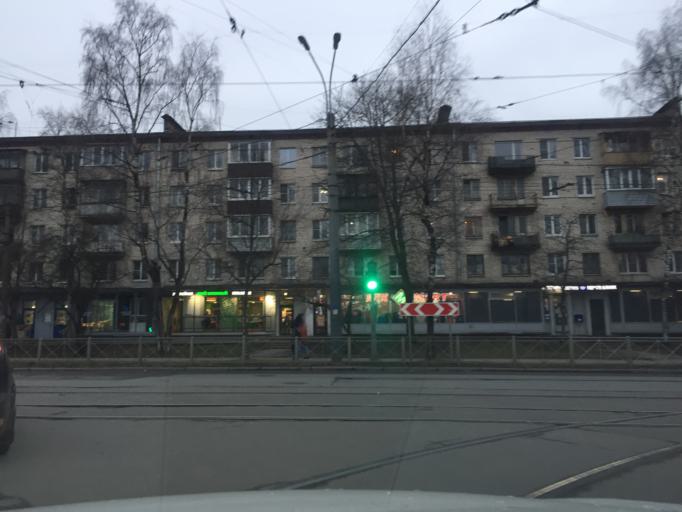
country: RU
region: St.-Petersburg
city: Sosnovka
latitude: 60.0165
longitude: 30.3679
